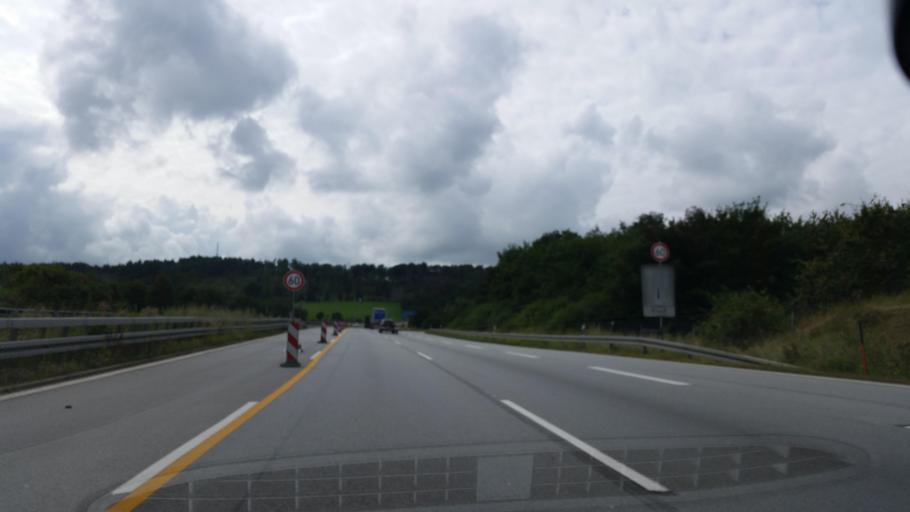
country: DE
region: Saxony
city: Rammenau
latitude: 51.1800
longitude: 14.1446
